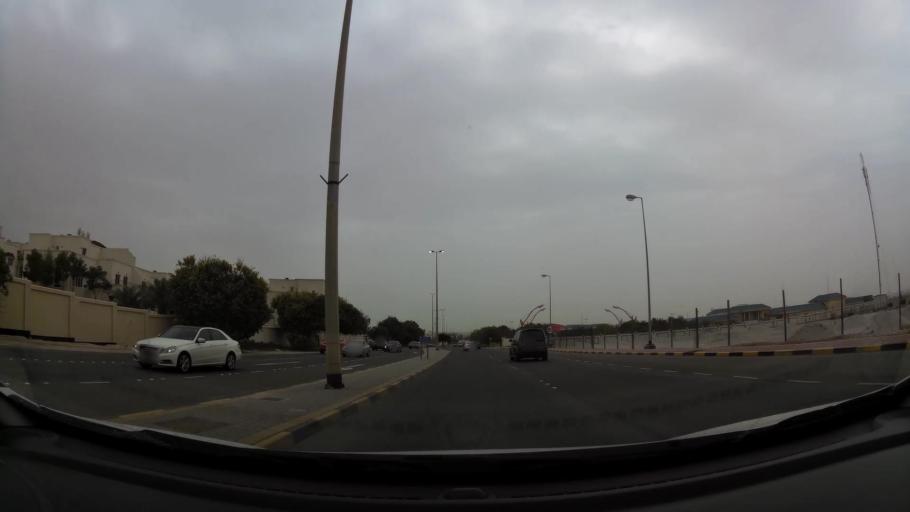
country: BH
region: Northern
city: Ar Rifa'
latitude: 26.1461
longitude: 50.5430
